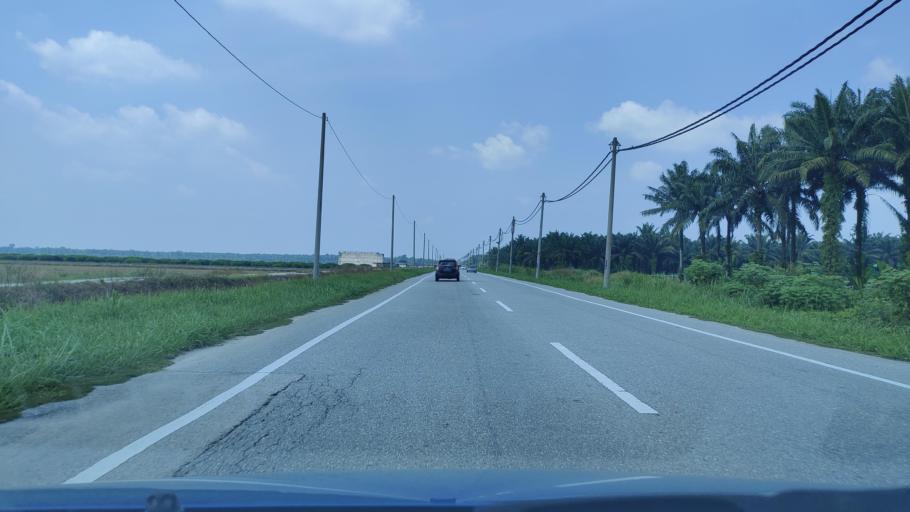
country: MY
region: Perak
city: Tapah Road
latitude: 4.0488
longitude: 101.1658
